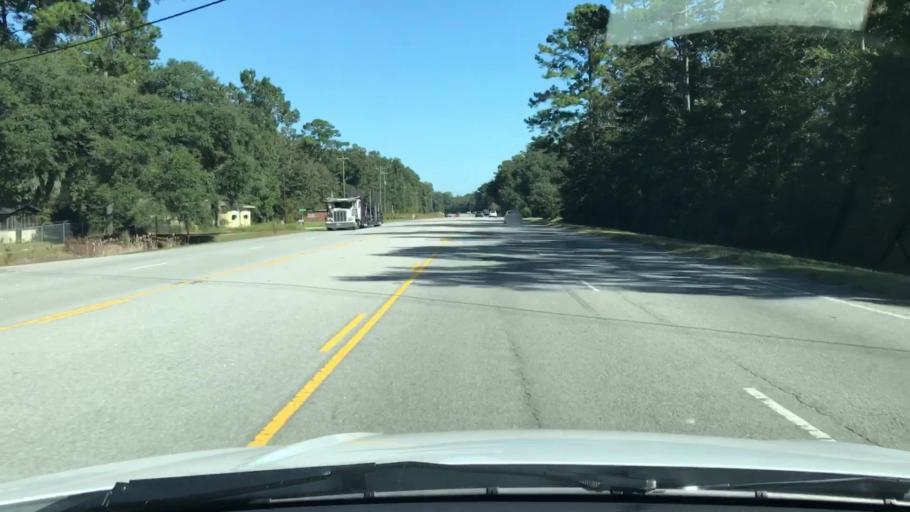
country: US
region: South Carolina
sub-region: Beaufort County
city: Bluffton
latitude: 32.3560
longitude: -80.8833
